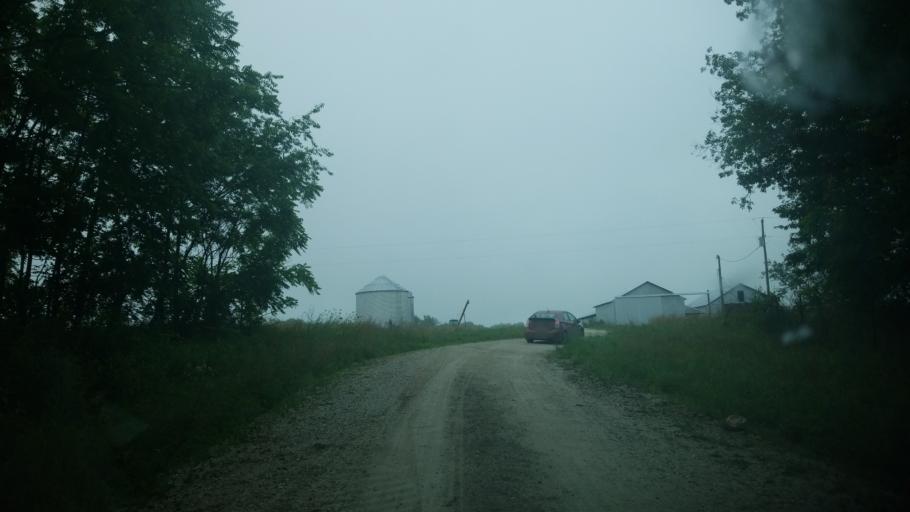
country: US
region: Missouri
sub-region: Pike County
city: Bowling Green
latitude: 39.3081
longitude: -91.2894
